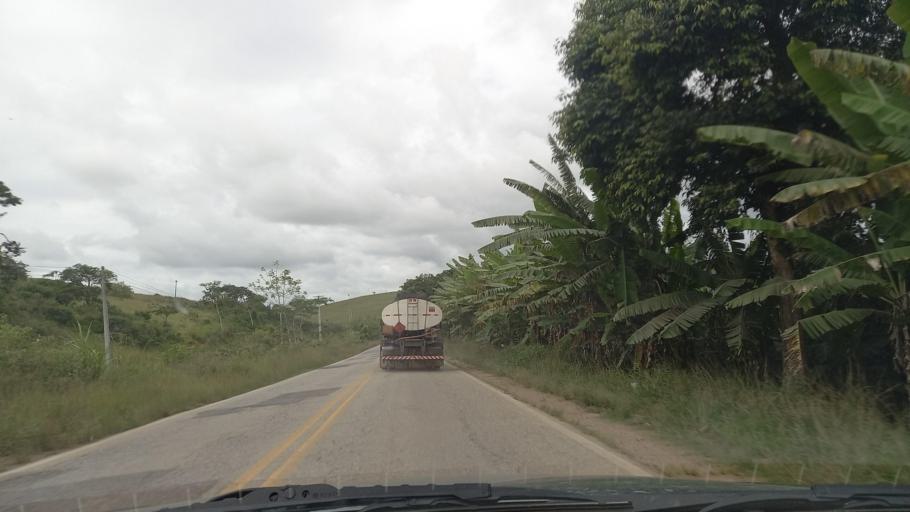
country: BR
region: Pernambuco
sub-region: Canhotinho
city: Canhotinho
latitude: -8.8717
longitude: -36.1974
